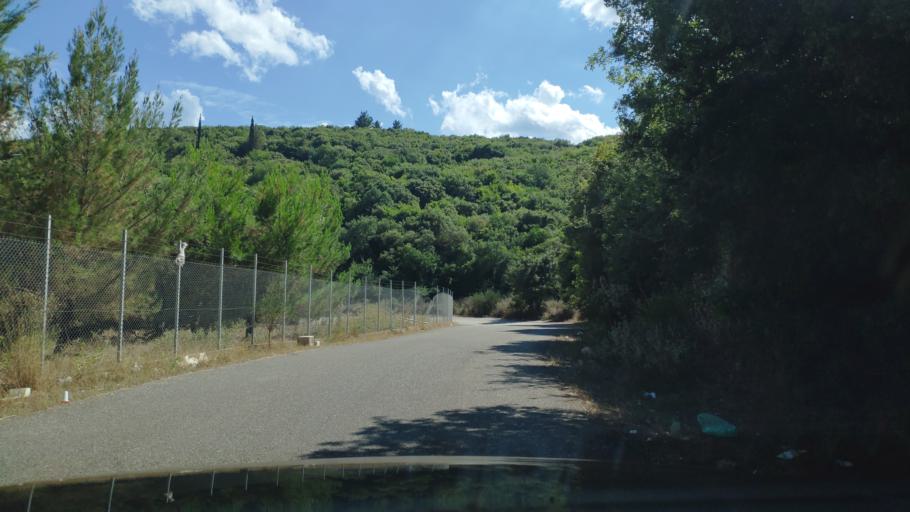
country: GR
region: West Greece
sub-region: Nomos Aitolias kai Akarnanias
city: Katouna
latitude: 38.7980
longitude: 21.1126
